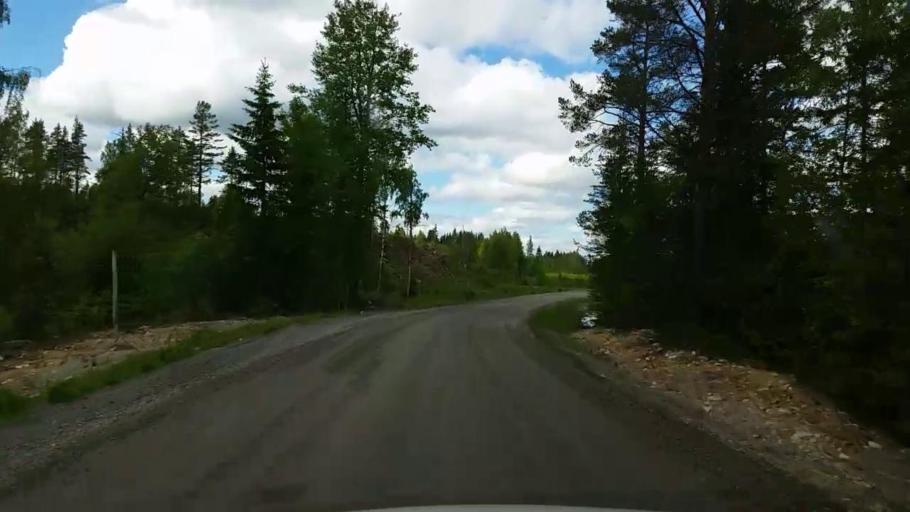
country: SE
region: Gaevleborg
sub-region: Bollnas Kommun
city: Vittsjo
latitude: 61.1703
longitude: 16.1547
